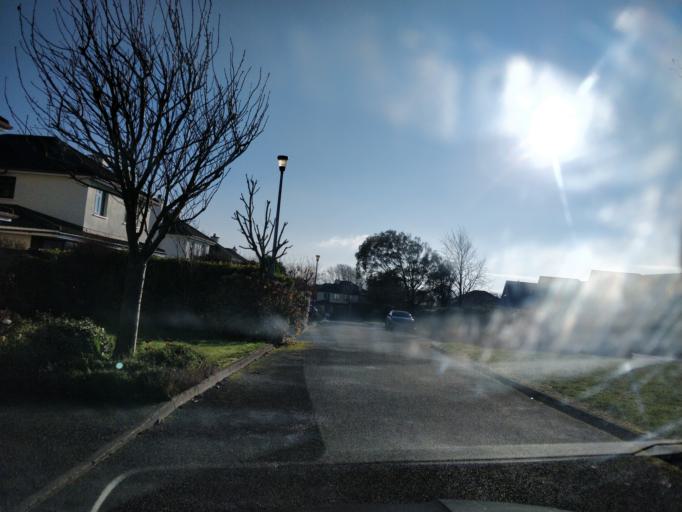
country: IE
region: Connaught
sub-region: County Galway
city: Bearna
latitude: 53.2619
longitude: -9.1218
